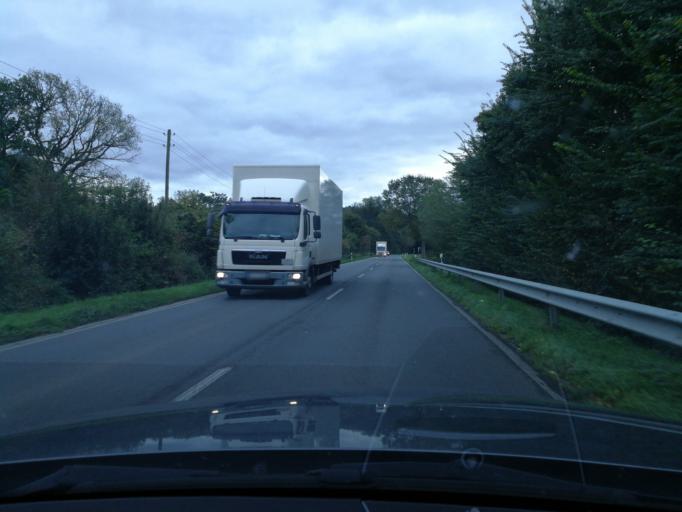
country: DE
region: North Rhine-Westphalia
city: Straelen
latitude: 51.4524
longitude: 6.2390
